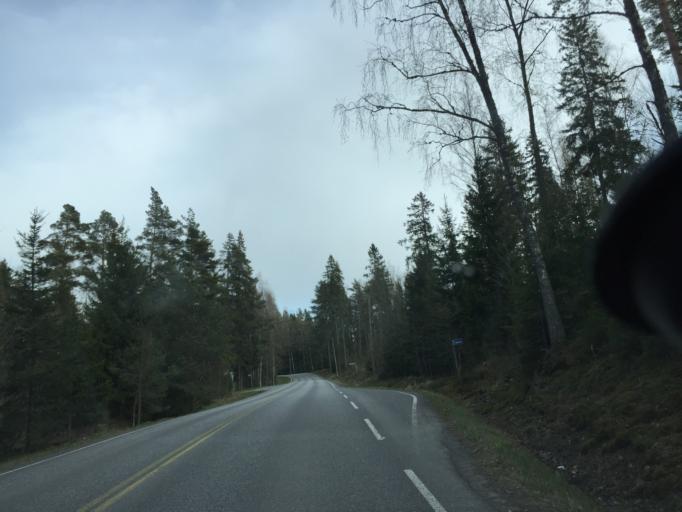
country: FI
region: Varsinais-Suomi
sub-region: Salo
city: Pernioe
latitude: 60.0066
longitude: 23.1143
